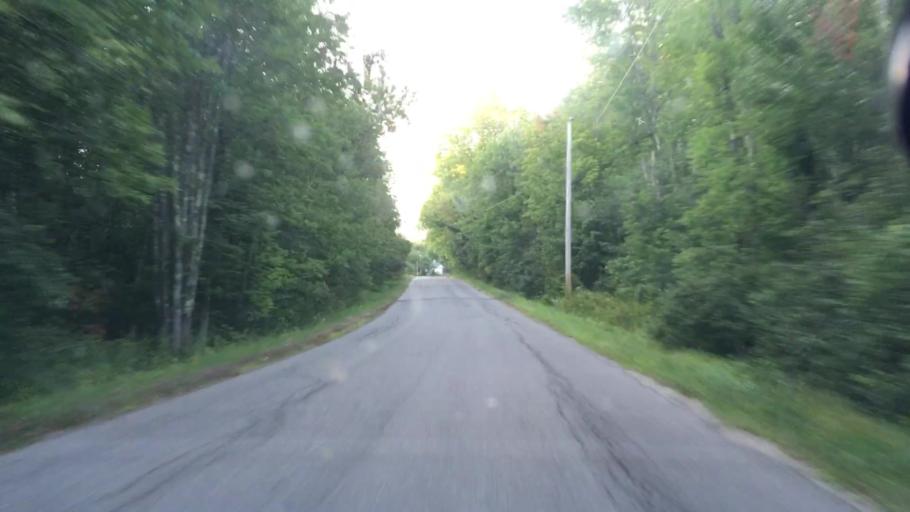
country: US
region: Maine
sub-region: Waldo County
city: Frankfort
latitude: 44.6698
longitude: -68.9259
